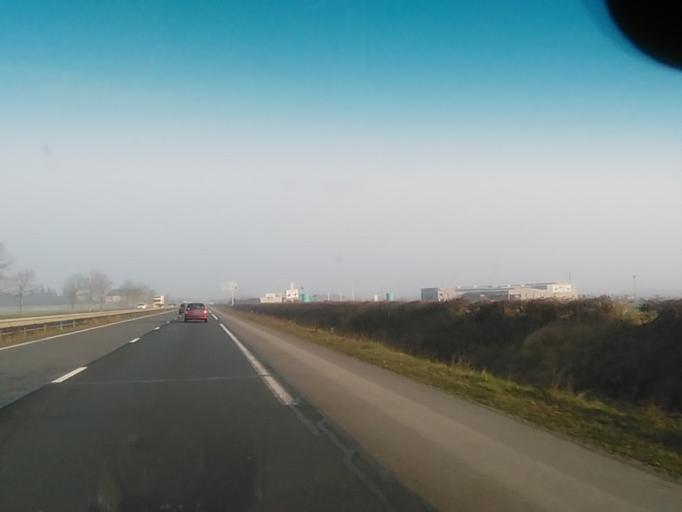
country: FR
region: Lower Normandy
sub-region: Departement du Calvados
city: Bretteville-sur-Laize
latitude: 49.0618
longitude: -0.2906
